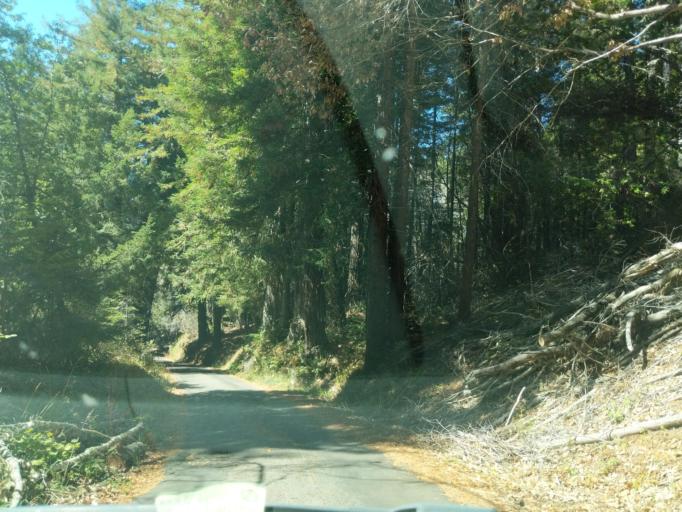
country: US
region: California
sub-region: Sonoma County
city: Monte Rio
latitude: 38.5238
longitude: -123.2324
